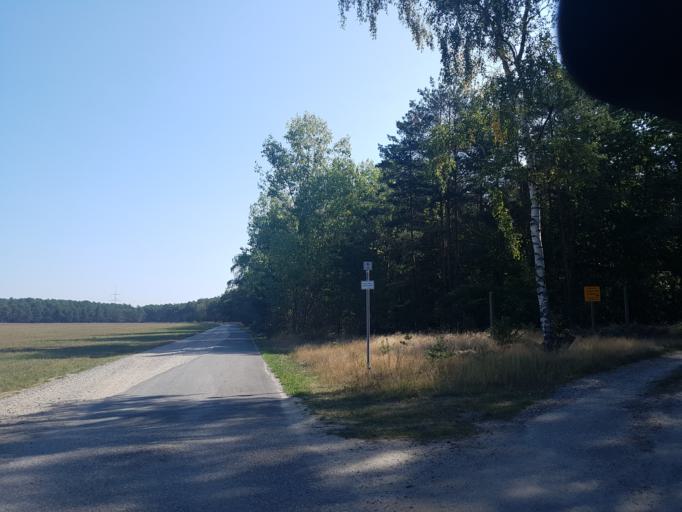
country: DE
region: Brandenburg
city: Finsterwalde
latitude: 51.6425
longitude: 13.7469
